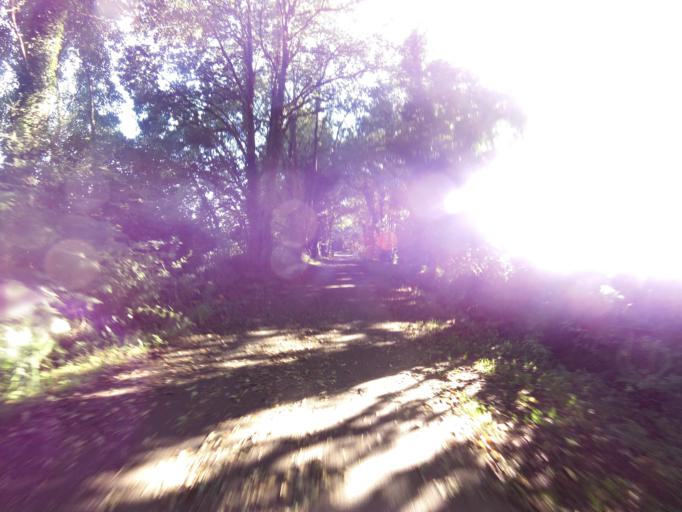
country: FR
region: Brittany
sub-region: Departement du Morbihan
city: Guillac
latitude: 47.9116
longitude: -2.4306
